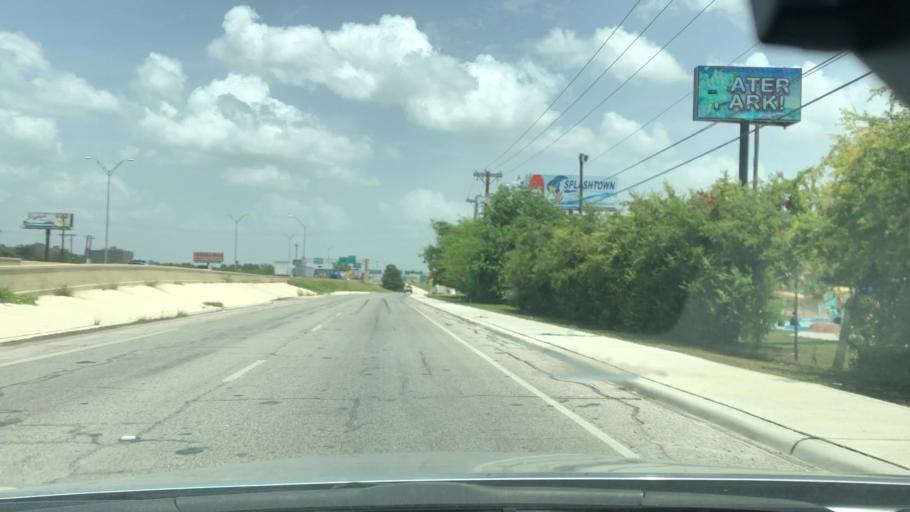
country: US
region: Texas
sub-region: Bexar County
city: Terrell Hills
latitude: 29.4479
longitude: -98.4266
